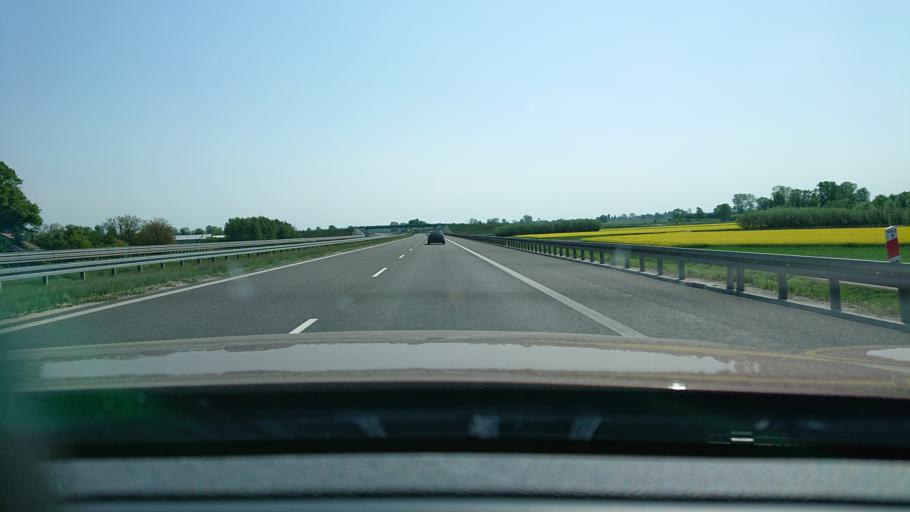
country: PL
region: Subcarpathian Voivodeship
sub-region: Powiat lancucki
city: Rogozno
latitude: 50.1115
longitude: 22.3726
